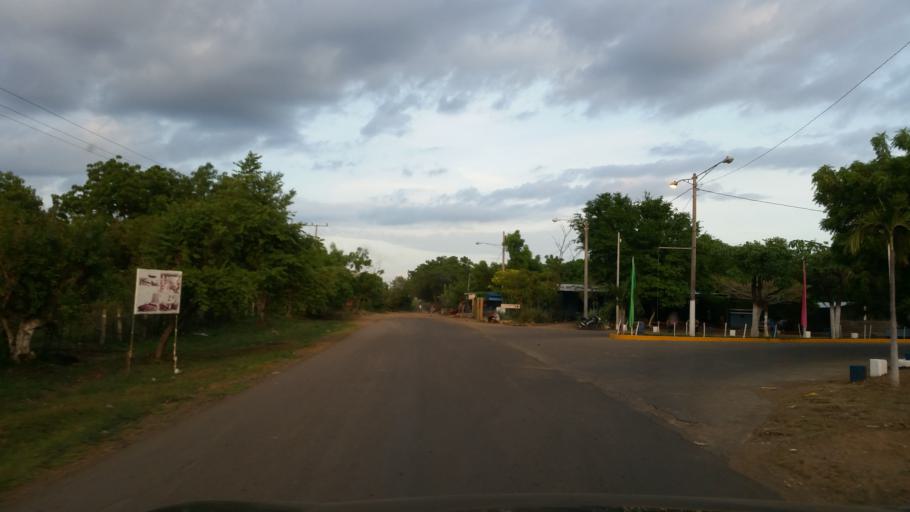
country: NI
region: Managua
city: Masachapa
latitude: 11.7758
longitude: -86.5052
